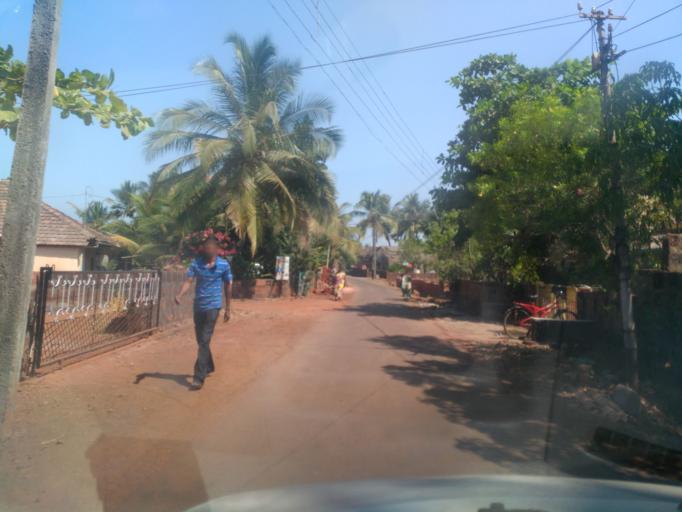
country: IN
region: Maharashtra
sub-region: Ratnagiri
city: Makhjan
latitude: 17.2393
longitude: 73.2707
